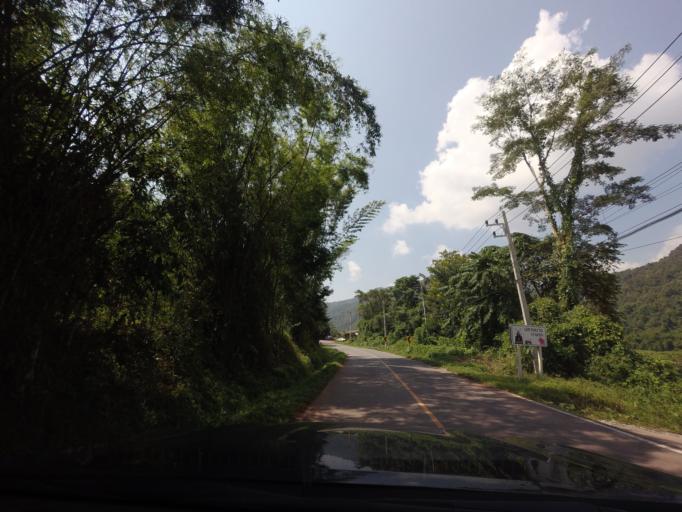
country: TH
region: Nan
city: Bo Kluea
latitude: 19.1347
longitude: 101.1514
